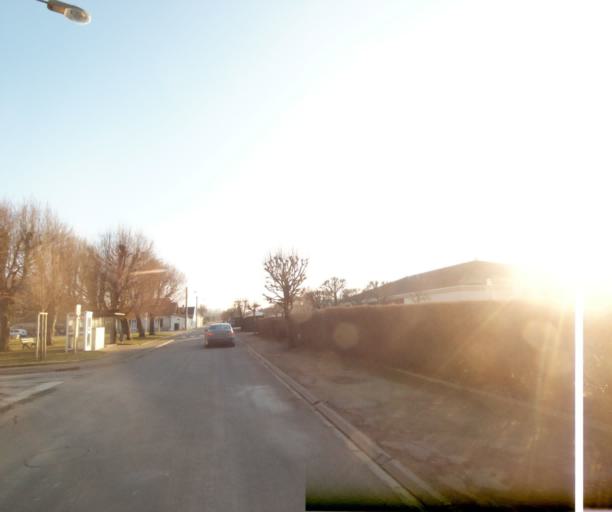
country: FR
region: Champagne-Ardenne
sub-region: Departement de la Haute-Marne
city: Bienville
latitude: 48.5817
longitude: 5.0454
